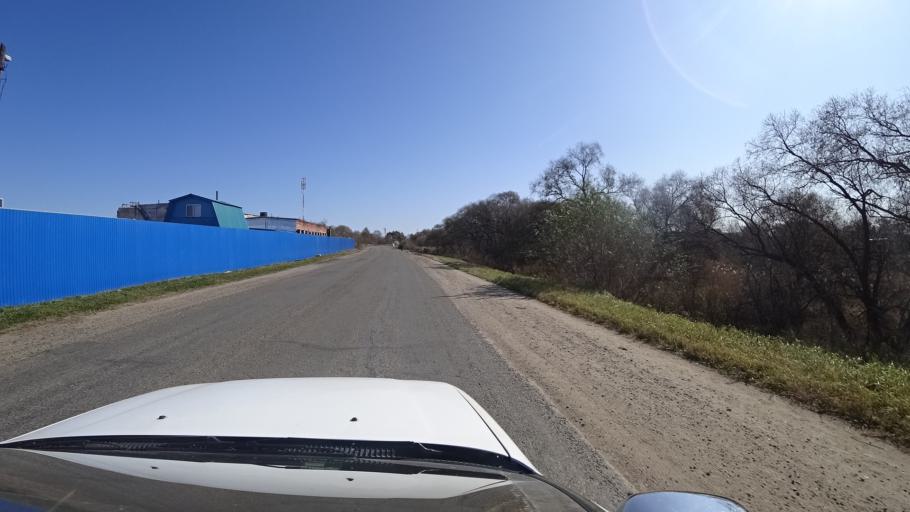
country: RU
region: Primorskiy
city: Dal'nerechensk
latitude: 45.9110
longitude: 133.7984
